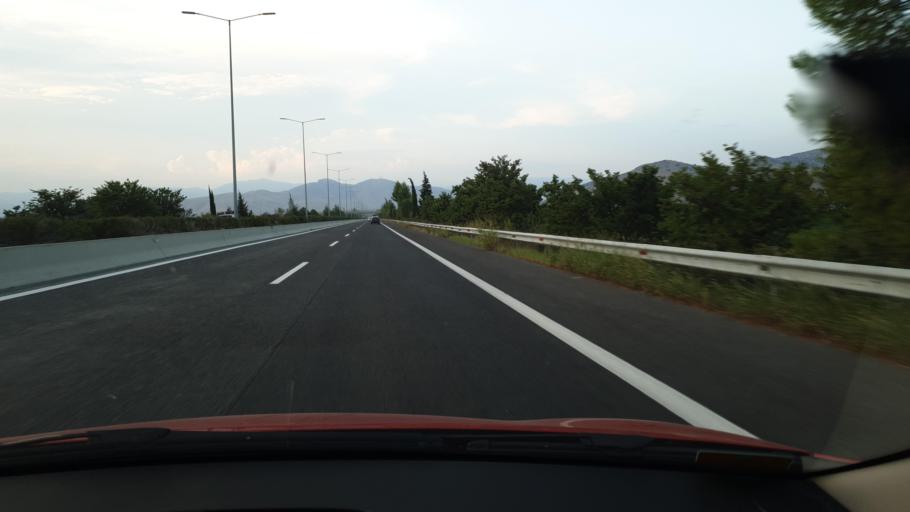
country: GR
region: Thessaly
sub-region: Nomos Larisis
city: Falani
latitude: 39.7123
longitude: 22.4837
